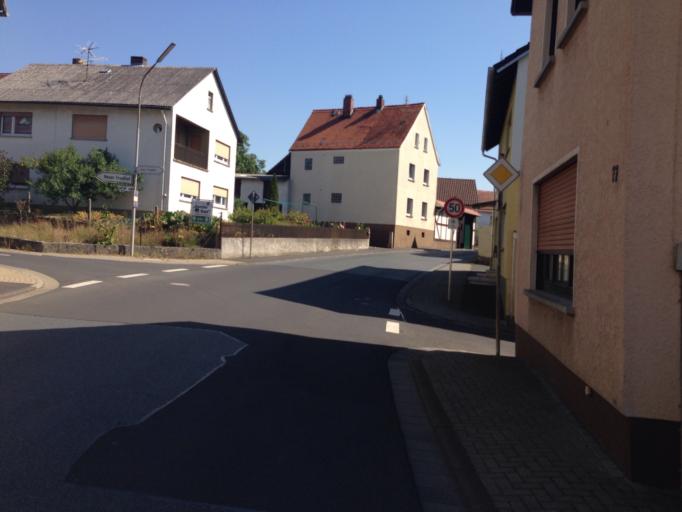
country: DE
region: Hesse
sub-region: Regierungsbezirk Giessen
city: Schoeffengrund
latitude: 50.5035
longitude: 8.5440
